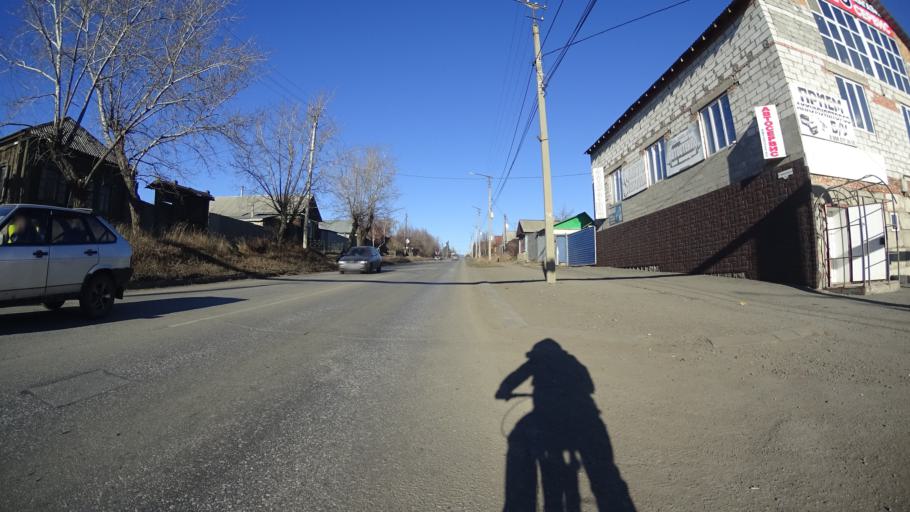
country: RU
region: Chelyabinsk
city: Troitsk
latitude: 54.1001
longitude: 61.5626
